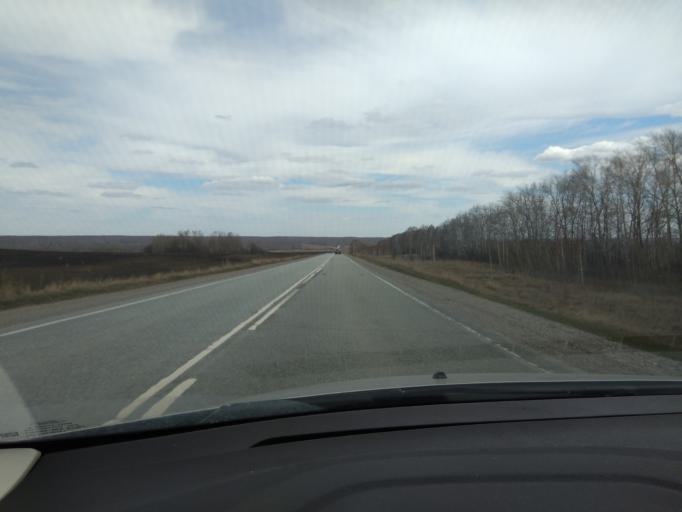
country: RU
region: Sverdlovsk
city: Yelanskiy
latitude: 56.7589
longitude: 62.3590
